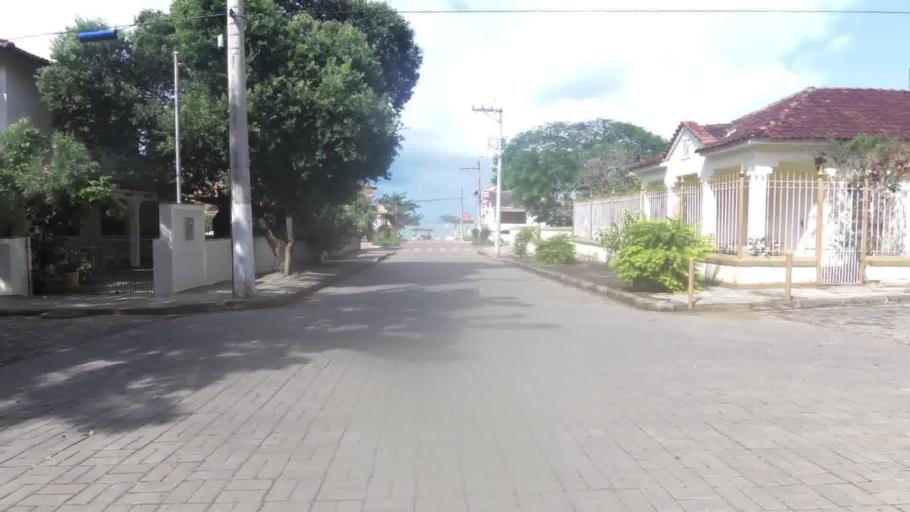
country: BR
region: Espirito Santo
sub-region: Piuma
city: Piuma
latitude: -20.8321
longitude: -40.6978
